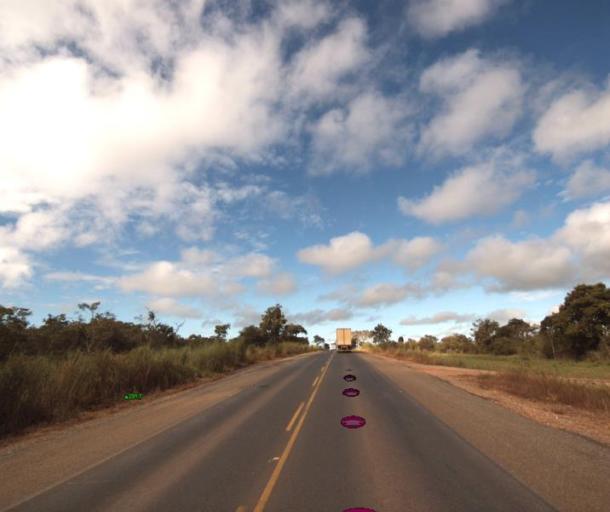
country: BR
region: Goias
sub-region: Uruacu
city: Uruacu
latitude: -14.7798
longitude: -49.2719
